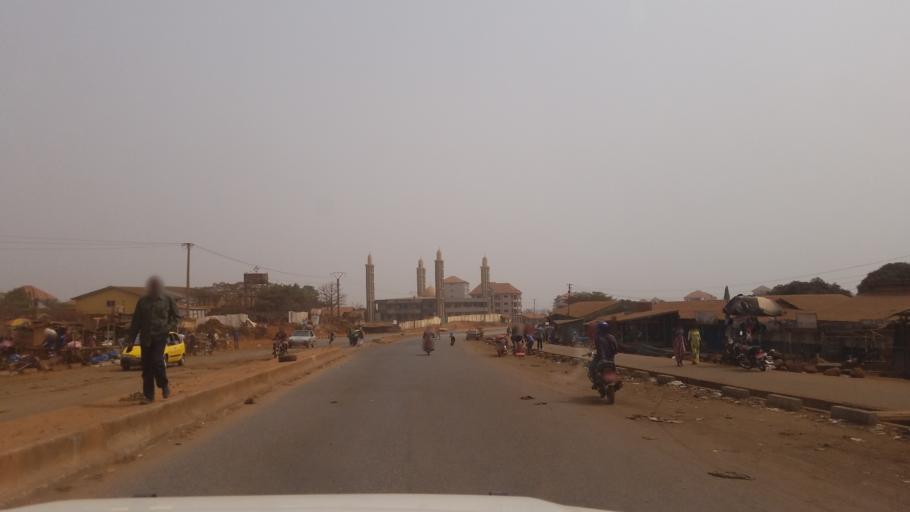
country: GN
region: Kindia
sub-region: Prefecture de Dubreka
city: Dubreka
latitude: 9.6819
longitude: -13.5337
